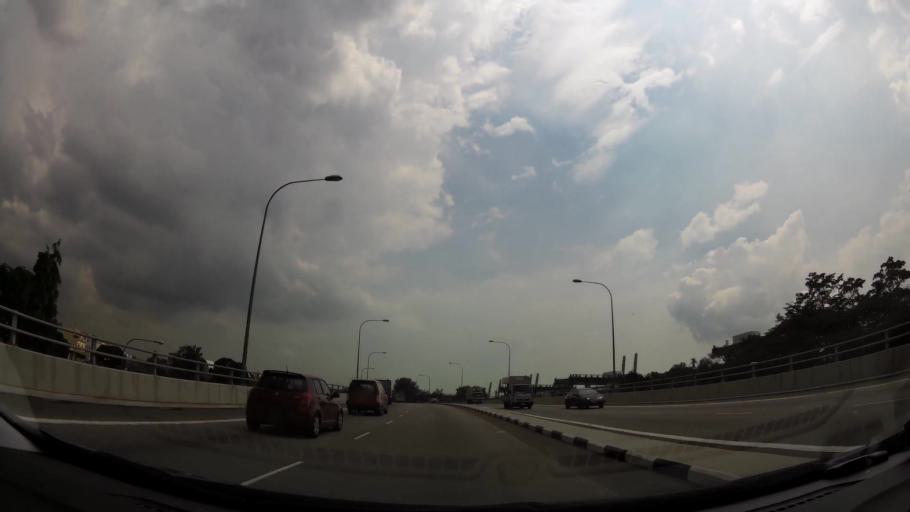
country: SG
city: Singapore
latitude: 1.2924
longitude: 103.7665
